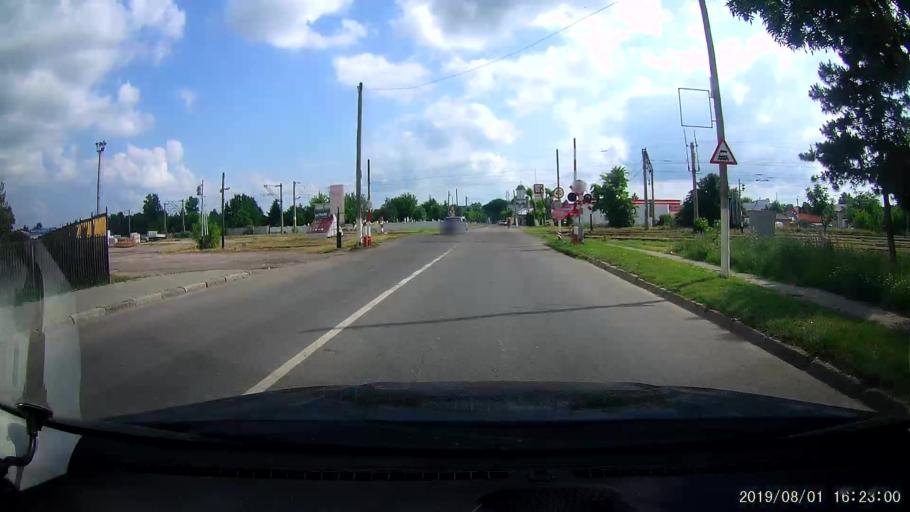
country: RO
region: Calarasi
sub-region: Municipiul Calarasi
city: Calarasi
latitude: 44.1995
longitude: 27.3364
